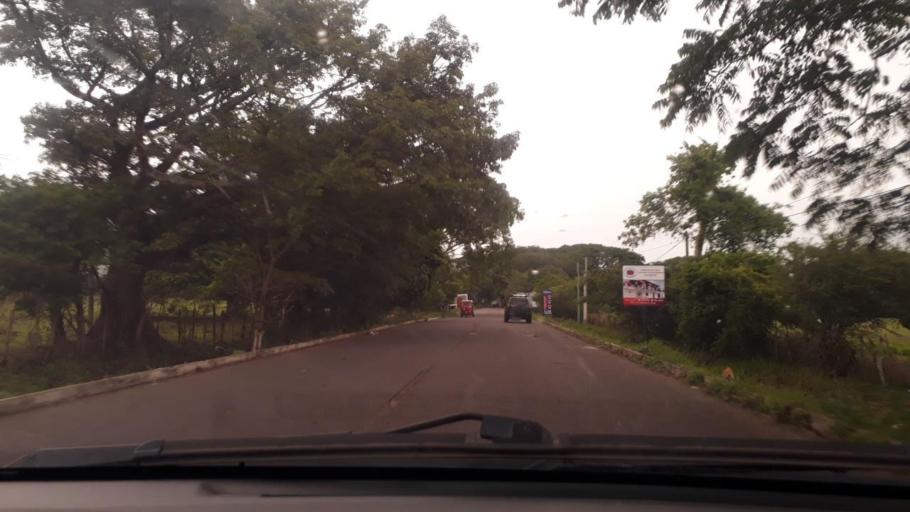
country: GT
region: Jutiapa
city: Jalpatagua
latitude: 14.1464
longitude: -90.0313
